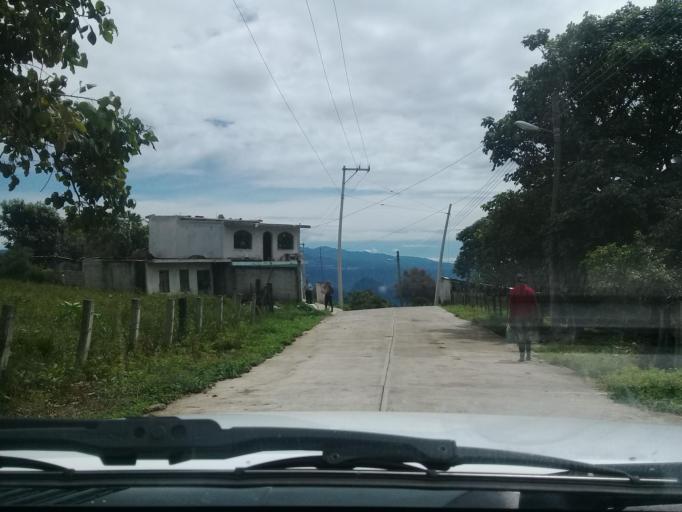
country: MX
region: Veracruz
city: Rafael Lucio
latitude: 19.5948
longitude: -96.9828
